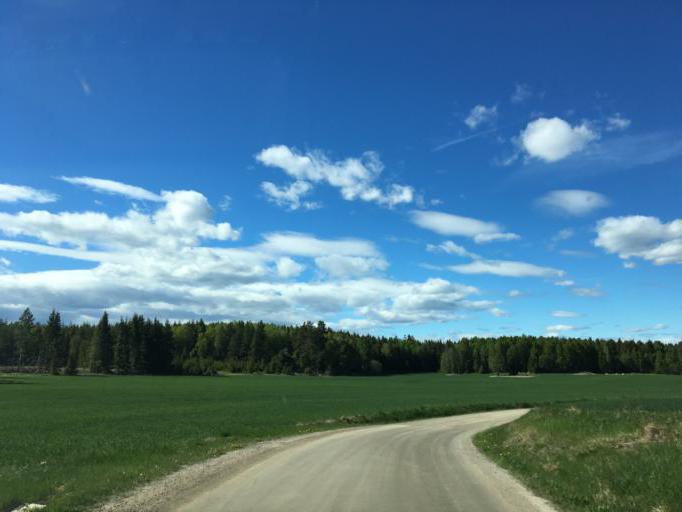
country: SE
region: Soedermanland
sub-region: Eskilstuna Kommun
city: Kvicksund
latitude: 59.3956
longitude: 16.2364
